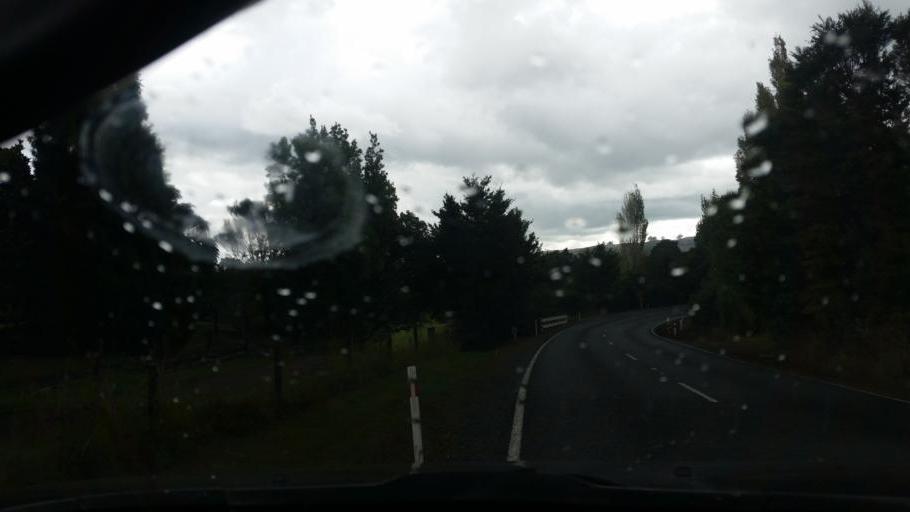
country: NZ
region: Northland
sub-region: Whangarei
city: Ruakaka
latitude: -35.9442
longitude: 174.2916
